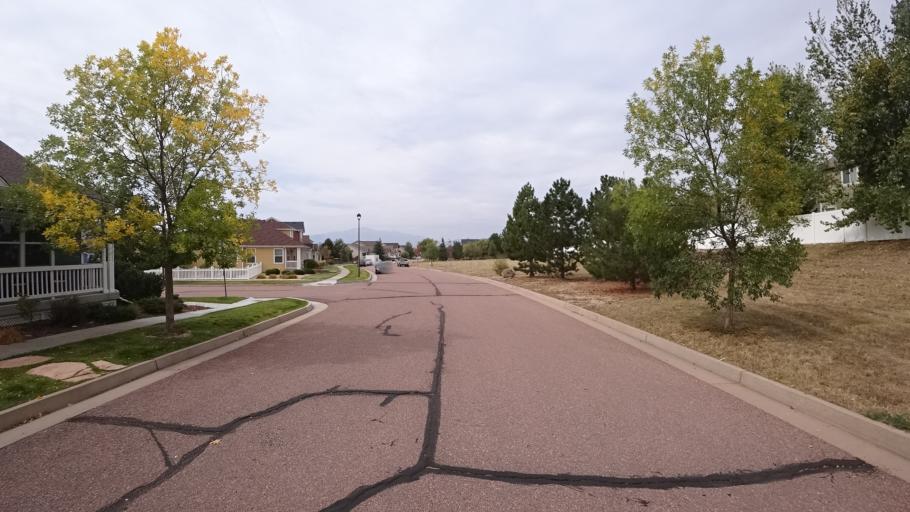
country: US
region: Colorado
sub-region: El Paso County
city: Cimarron Hills
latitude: 38.9158
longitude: -104.6859
